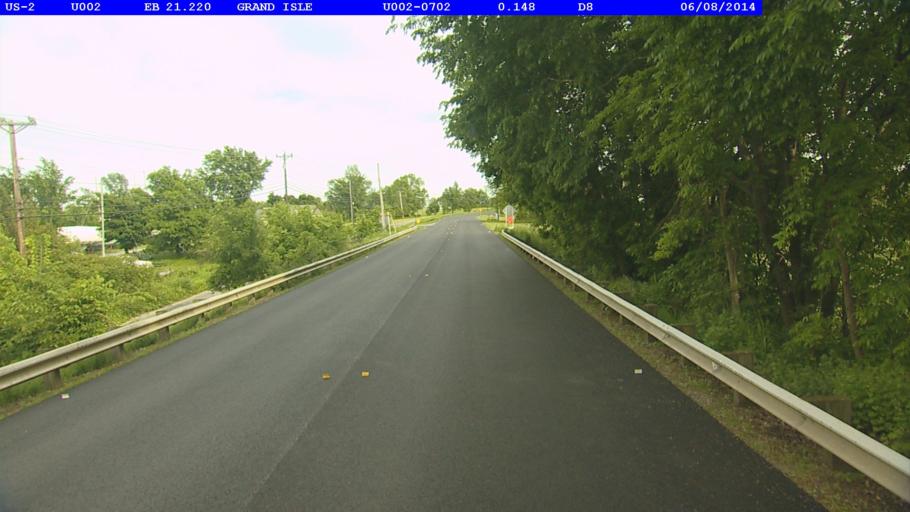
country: US
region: Vermont
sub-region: Grand Isle County
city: North Hero
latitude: 44.7645
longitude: -73.2880
